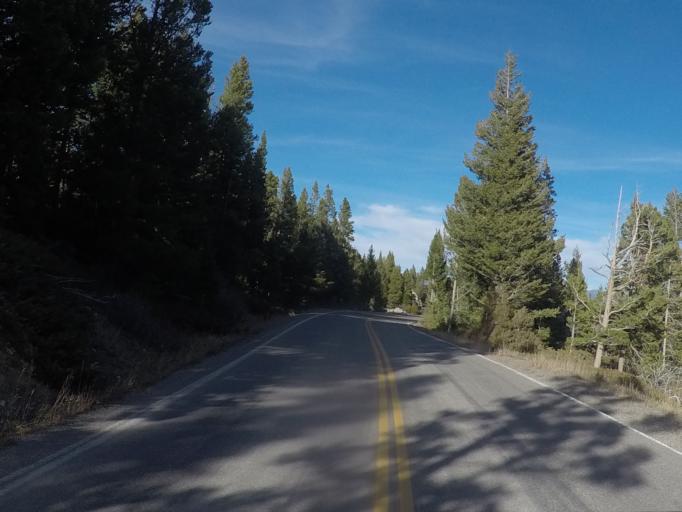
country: US
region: Montana
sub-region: Gallatin County
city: West Yellowstone
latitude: 44.9407
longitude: -110.7185
